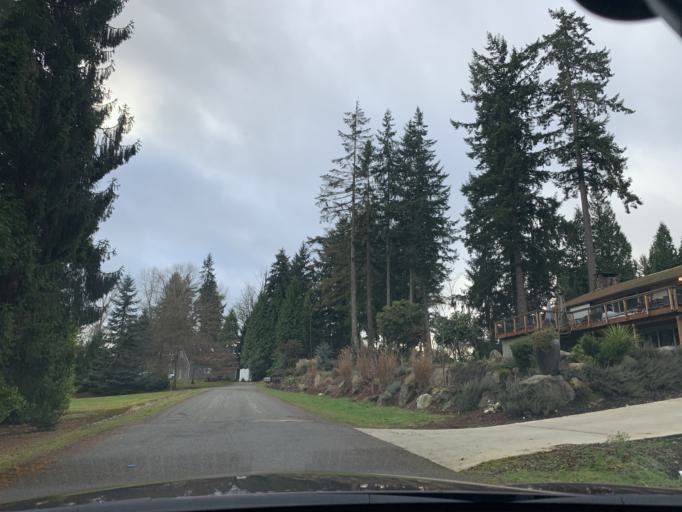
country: US
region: Washington
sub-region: King County
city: Kingsgate
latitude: 47.7364
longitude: -122.1664
